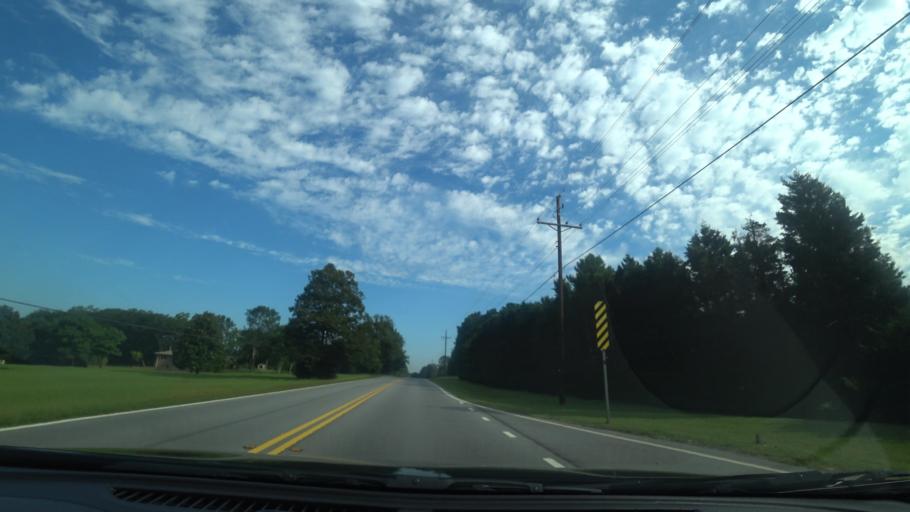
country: US
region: Georgia
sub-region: Rockdale County
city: Lakeview Estates
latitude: 33.7578
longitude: -83.9830
